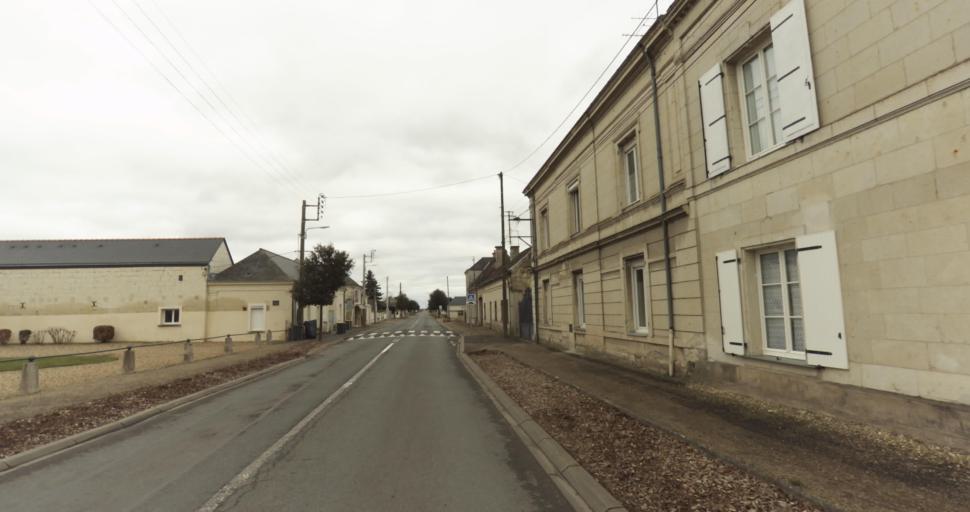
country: FR
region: Pays de la Loire
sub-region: Departement de Maine-et-Loire
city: Allonnes
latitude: 47.2926
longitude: 0.0267
